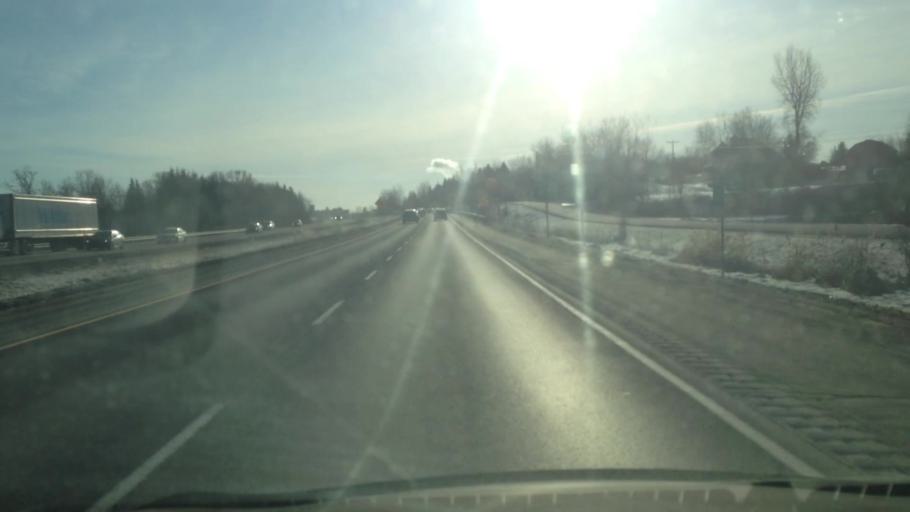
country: CA
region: Quebec
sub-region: Laurentides
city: Prevost
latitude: 45.8168
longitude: -74.0517
